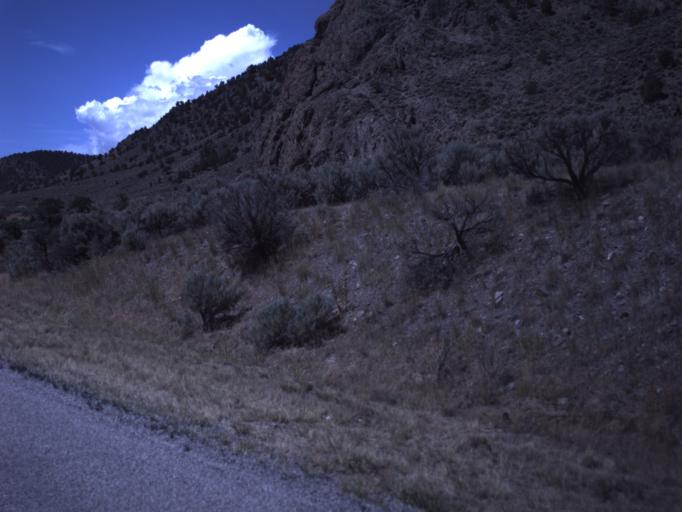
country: US
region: Utah
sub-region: Piute County
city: Junction
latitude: 38.0759
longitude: -112.3404
